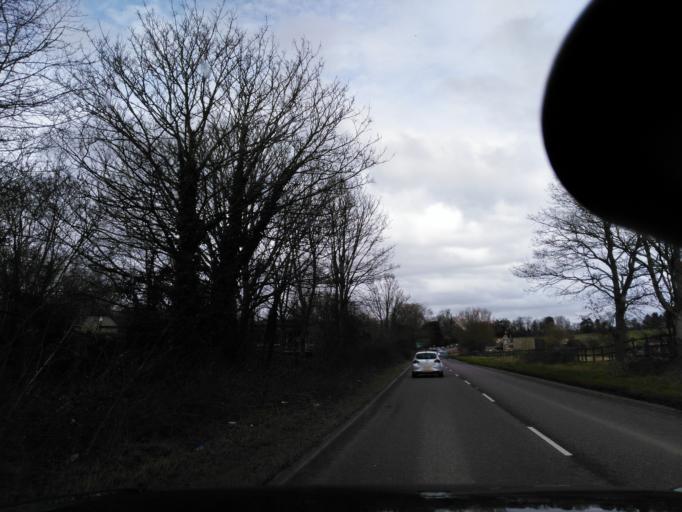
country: GB
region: England
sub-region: Wiltshire
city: Lacock
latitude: 51.4254
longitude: -2.1277
